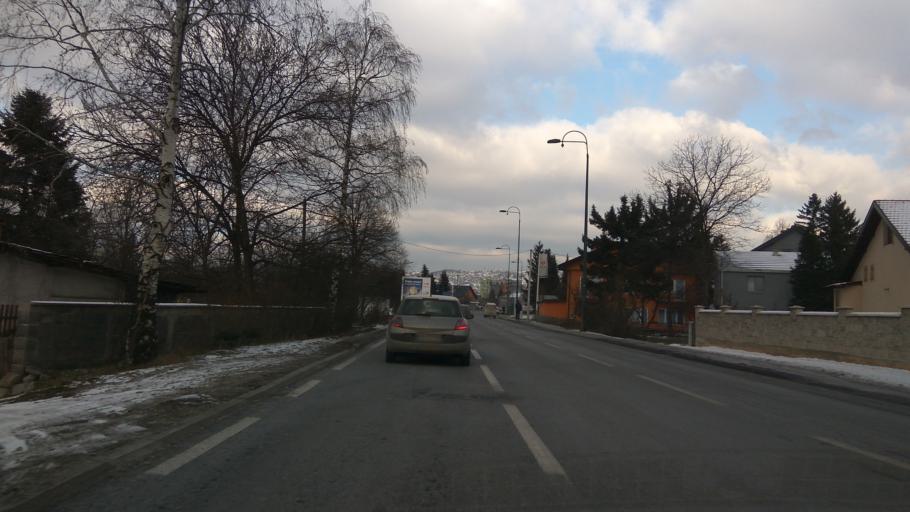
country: BA
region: Federation of Bosnia and Herzegovina
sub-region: Kanton Sarajevo
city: Sarajevo
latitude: 43.8355
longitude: 18.3159
